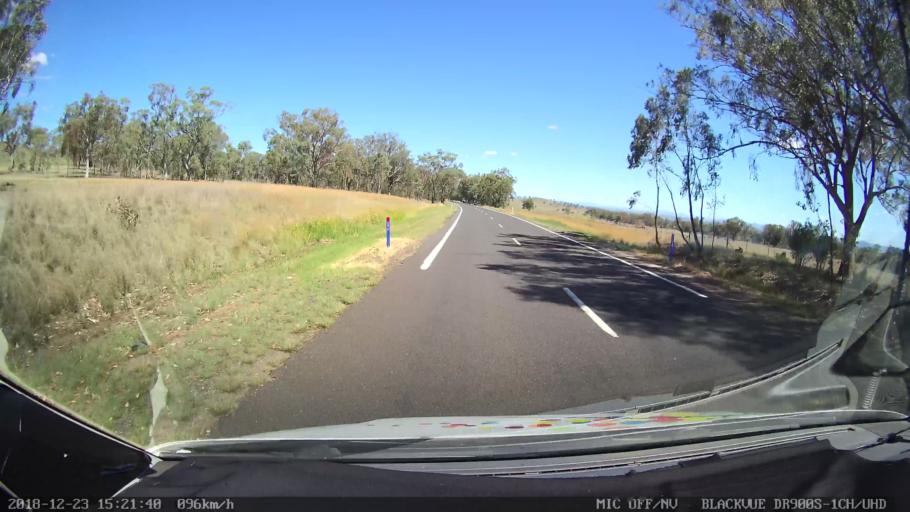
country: AU
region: New South Wales
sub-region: Tamworth Municipality
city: Manilla
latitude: -30.8594
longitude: 150.7982
